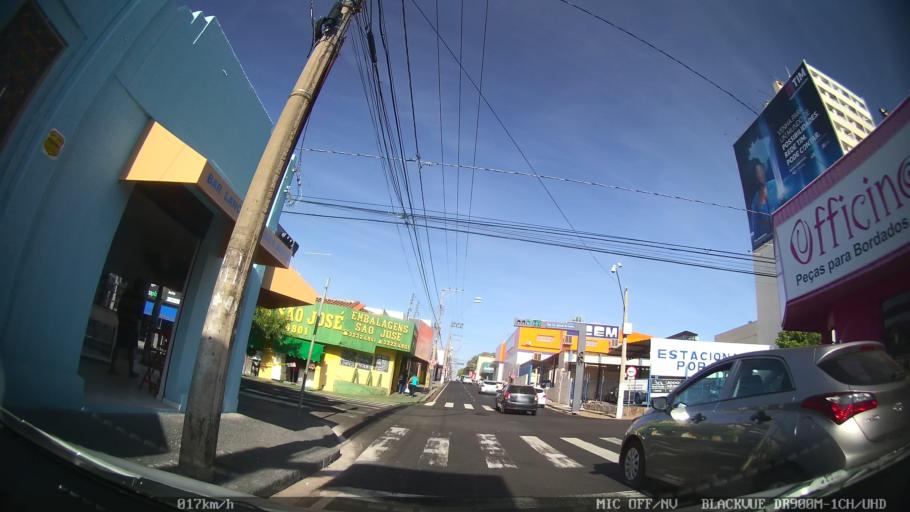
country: BR
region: Sao Paulo
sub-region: Sao Jose Do Rio Preto
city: Sao Jose do Rio Preto
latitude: -20.8082
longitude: -49.3800
